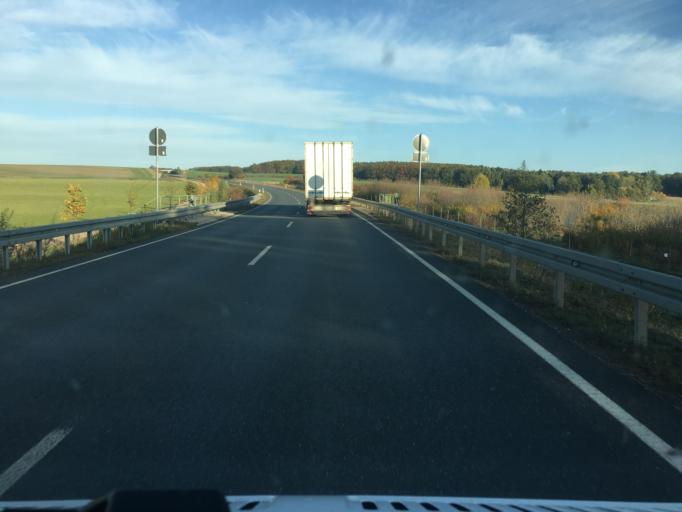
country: DE
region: Saxony
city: Lichtentanne
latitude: 50.7166
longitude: 12.4212
